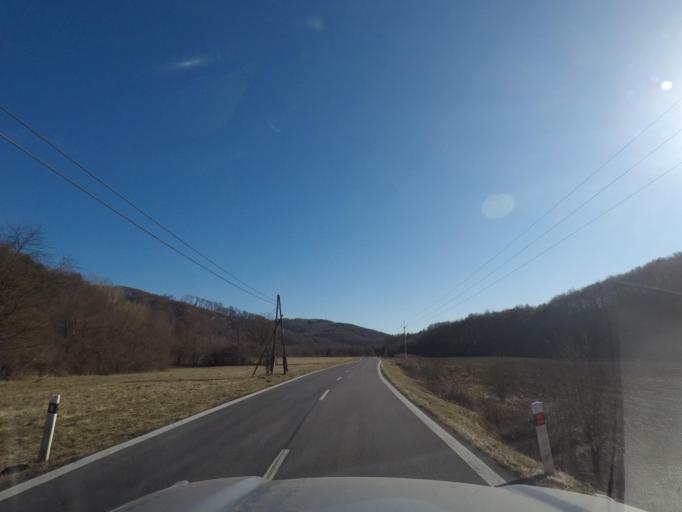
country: SK
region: Presovsky
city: Snina
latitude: 49.1174
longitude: 22.0746
